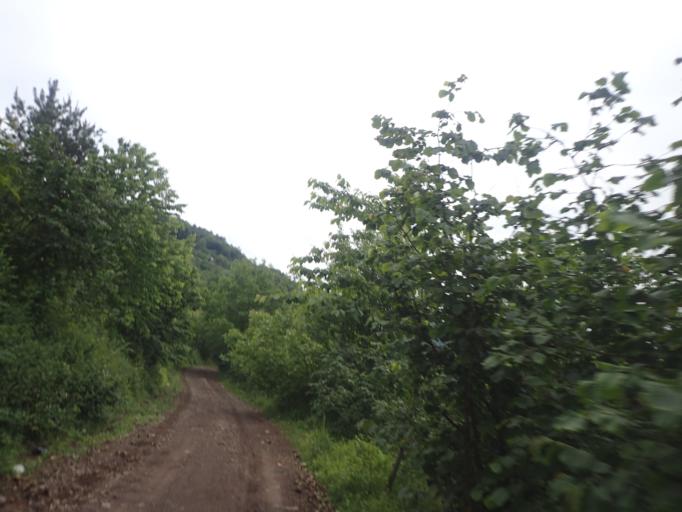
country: TR
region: Samsun
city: Salipazari
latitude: 40.9340
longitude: 36.9138
